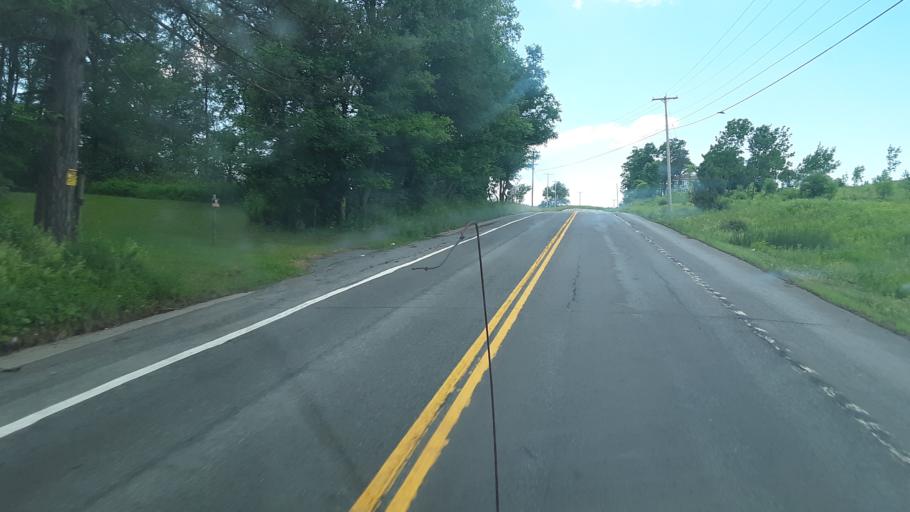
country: US
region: New York
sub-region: Oneida County
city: Rome
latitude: 43.3766
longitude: -75.4848
